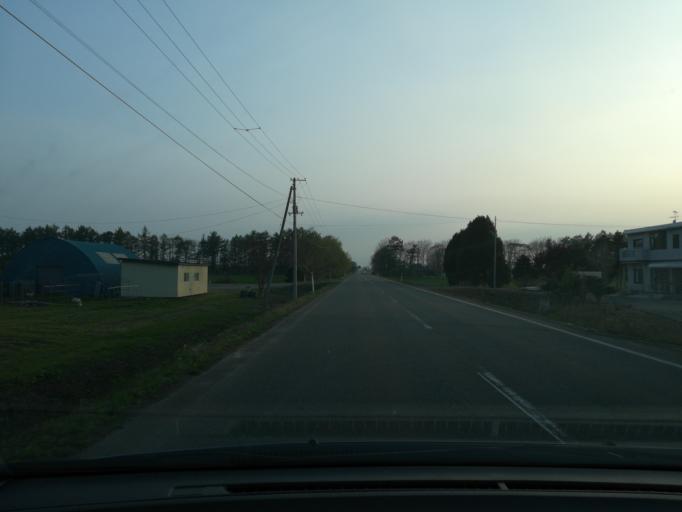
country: JP
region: Hokkaido
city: Ebetsu
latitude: 43.0916
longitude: 141.6355
